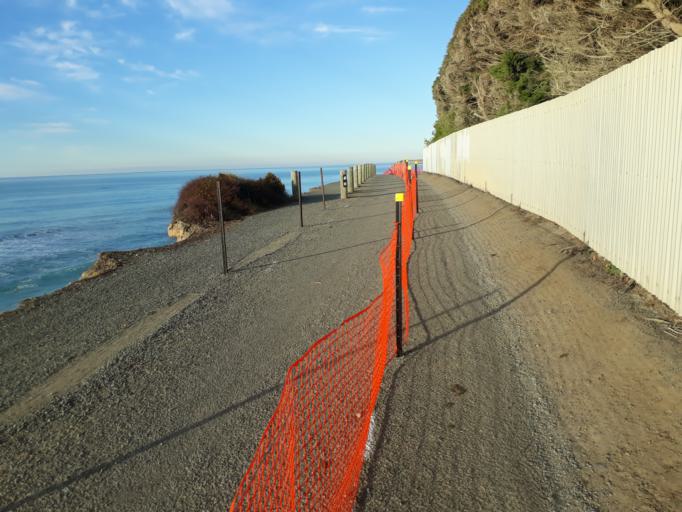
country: NZ
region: Canterbury
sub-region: Timaru District
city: Timaru
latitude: -44.4141
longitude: 171.2645
